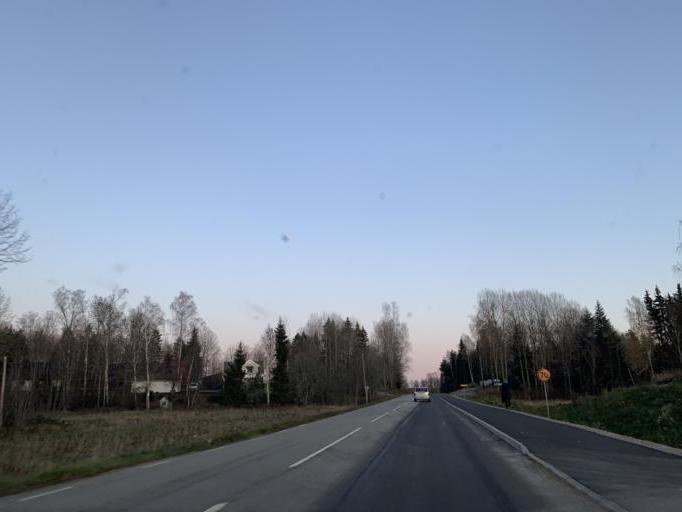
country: SE
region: OErebro
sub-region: Orebro Kommun
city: Hovsta
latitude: 59.3150
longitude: 15.3099
